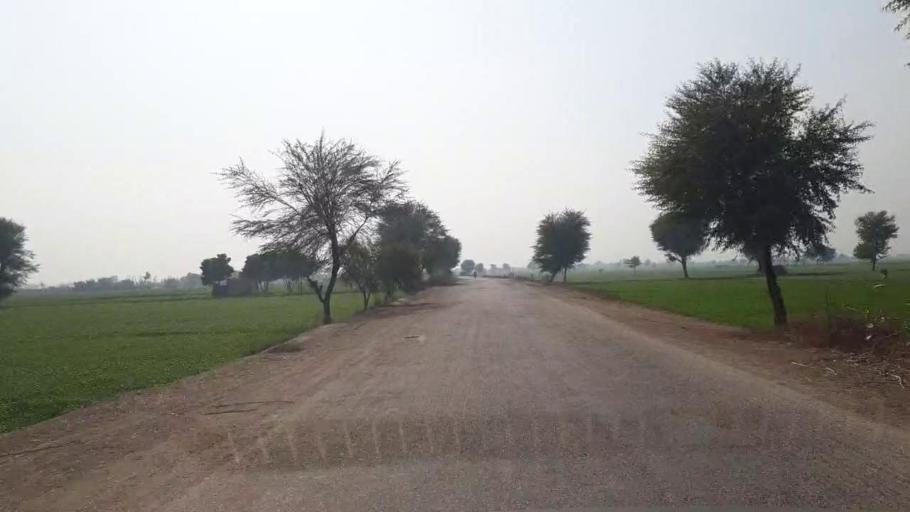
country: PK
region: Sindh
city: Hala
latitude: 25.8751
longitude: 68.4330
